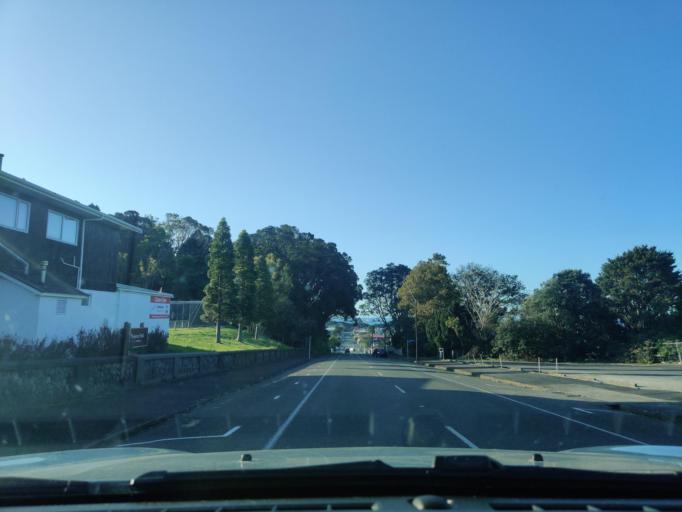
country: NZ
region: Taranaki
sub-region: New Plymouth District
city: New Plymouth
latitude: -39.0652
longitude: 174.0651
